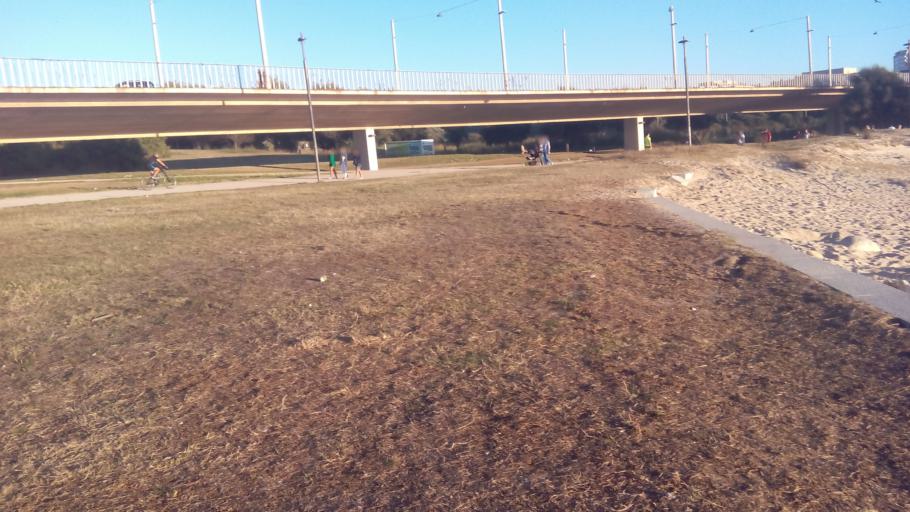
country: PT
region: Porto
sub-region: Matosinhos
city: Matosinhos
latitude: 41.1706
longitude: -8.6875
